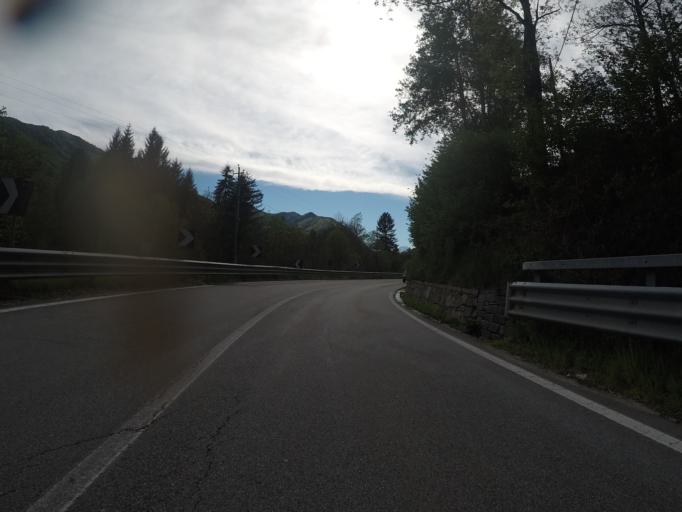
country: IT
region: Piedmont
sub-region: Provincia Verbano-Cusio-Ossola
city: Villette
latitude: 46.1280
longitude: 8.5269
